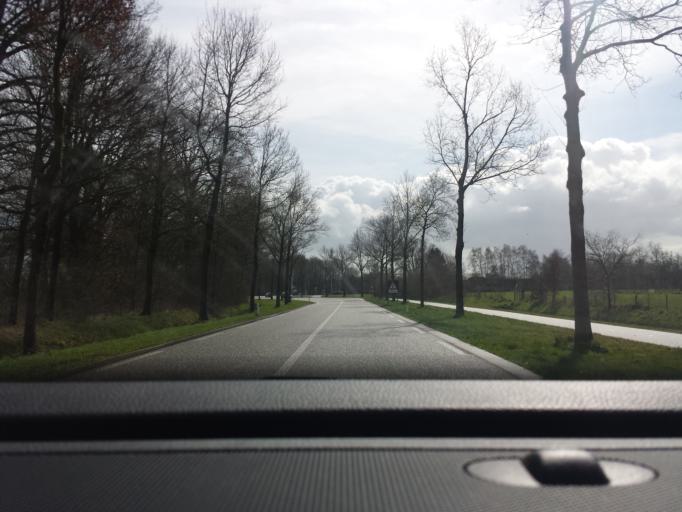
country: NL
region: Gelderland
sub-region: Oude IJsselstreek
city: Varsseveld
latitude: 51.9536
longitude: 6.4571
